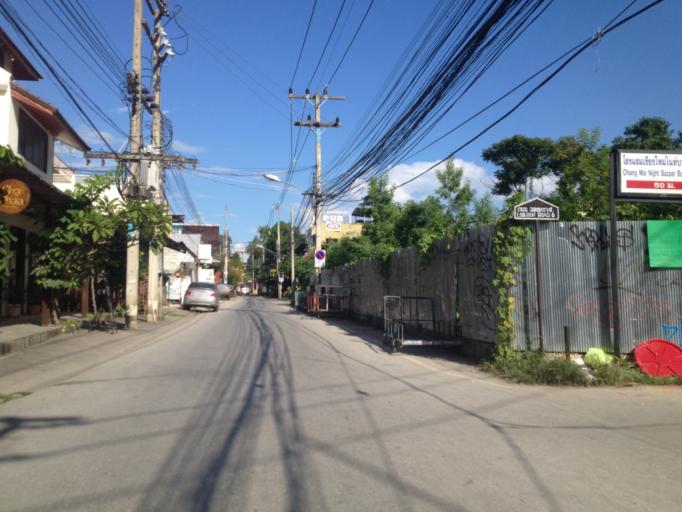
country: TH
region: Chiang Mai
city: Chiang Mai
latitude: 18.7839
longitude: 99.0017
